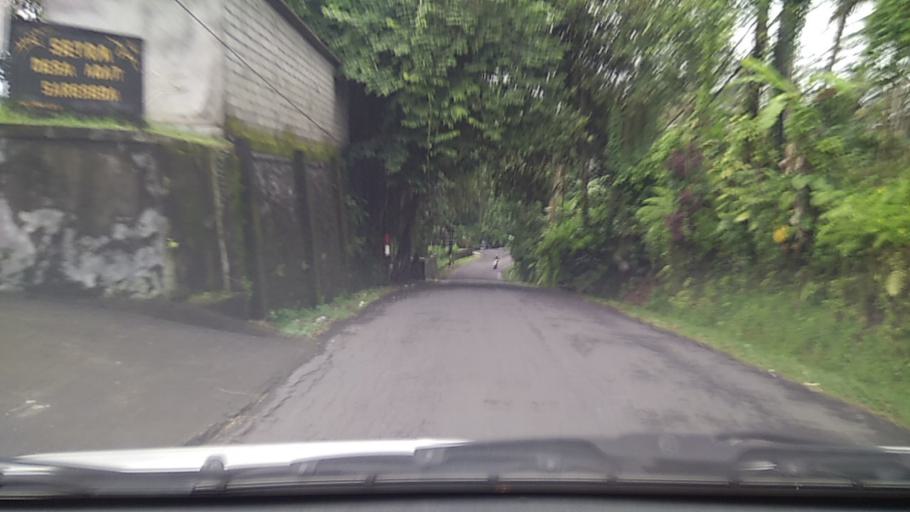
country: ID
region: Bali
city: Banjar Manukayaanyar
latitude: -8.4190
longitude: 115.3085
